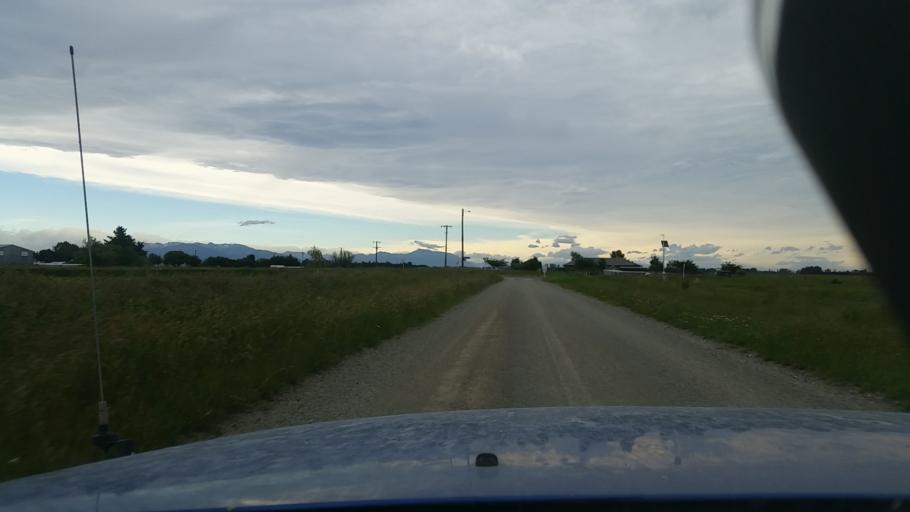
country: NZ
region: Canterbury
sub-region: Ashburton District
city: Tinwald
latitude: -43.9768
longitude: 171.5083
